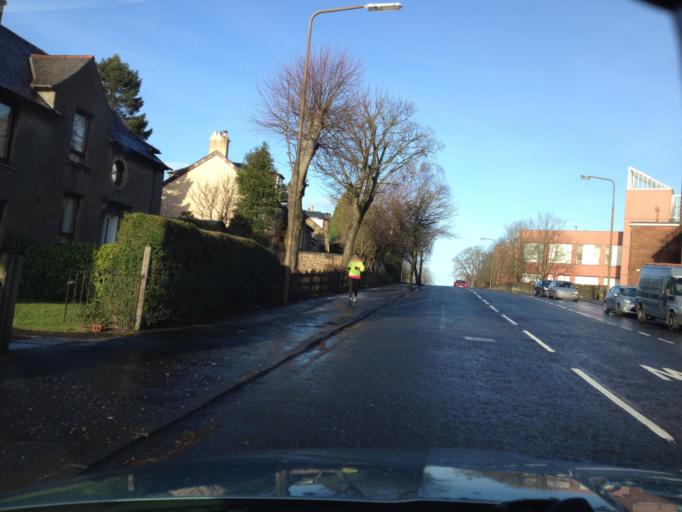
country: GB
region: Scotland
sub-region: West Lothian
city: Bathgate
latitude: 55.8981
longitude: -3.6324
